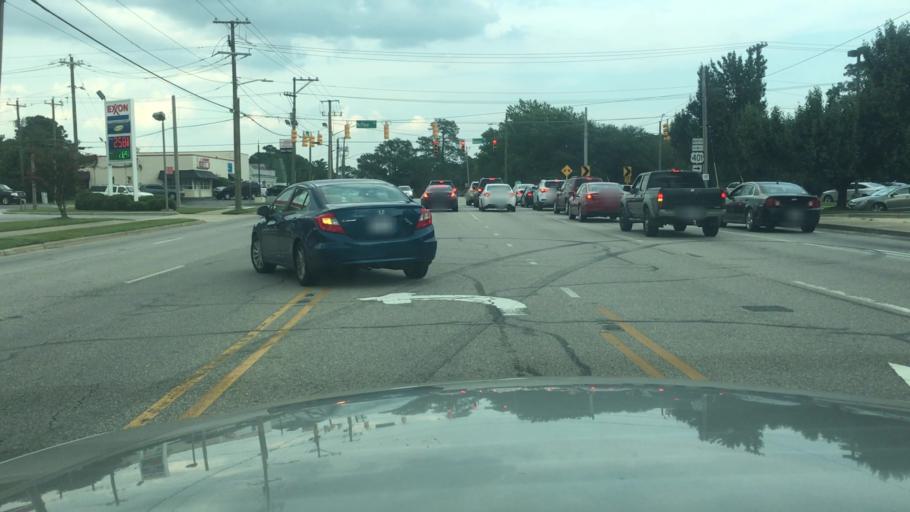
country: US
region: North Carolina
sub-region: Cumberland County
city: Fayetteville
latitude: 35.0460
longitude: -78.9201
